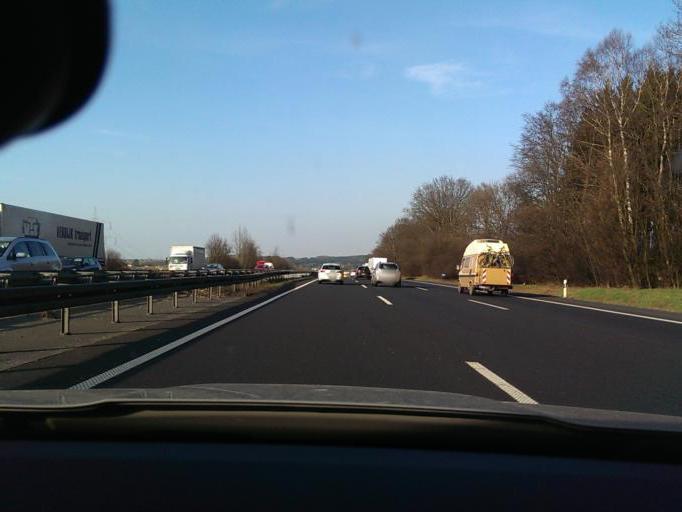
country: DE
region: Hesse
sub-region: Regierungsbezirk Kassel
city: Fuldatal
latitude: 51.3378
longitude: 9.5904
